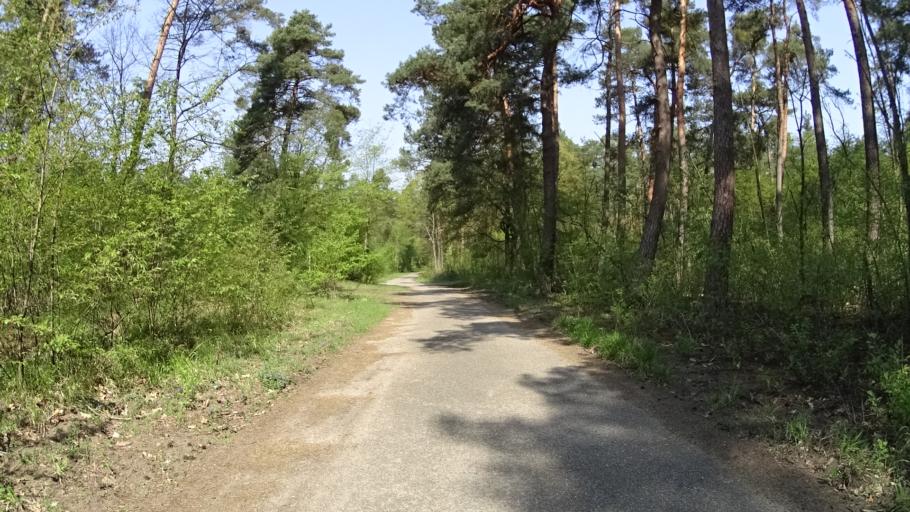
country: DE
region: Hesse
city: Viernheim
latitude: 49.5505
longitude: 8.5231
